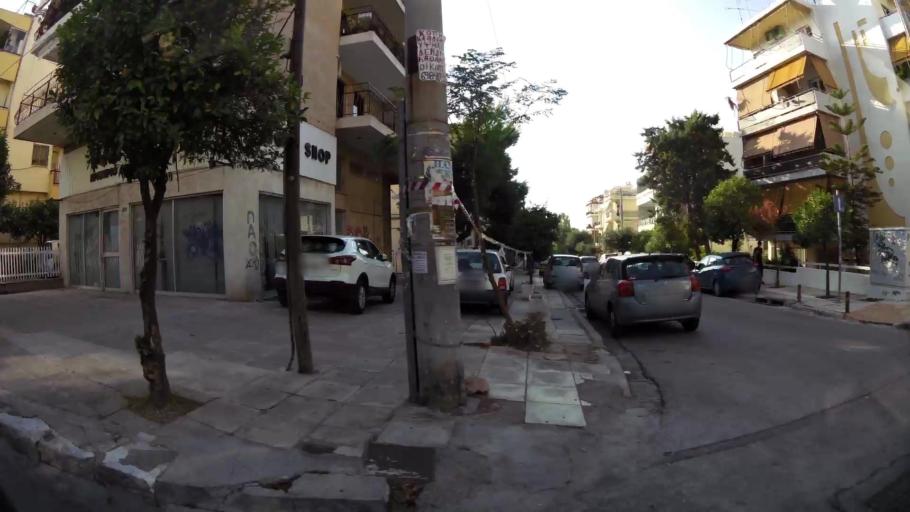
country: GR
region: Attica
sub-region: Nomarchia Athinas
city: Argyroupoli
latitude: 37.8936
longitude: 23.7533
